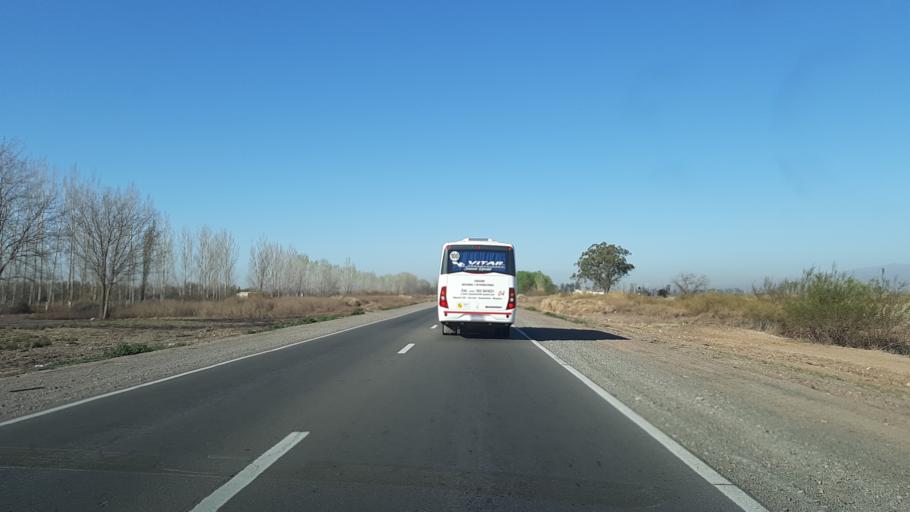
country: AR
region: Mendoza
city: General Lavalle
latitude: -32.6929
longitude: -68.6684
